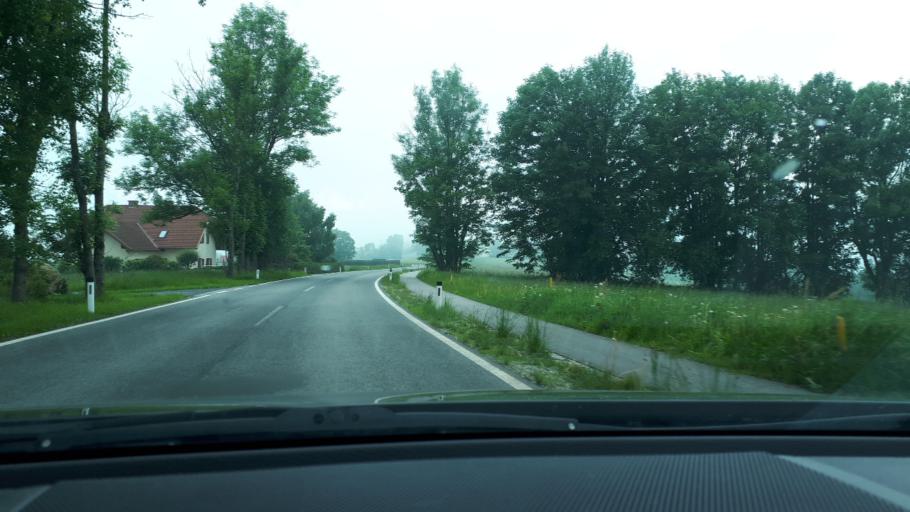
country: AT
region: Carinthia
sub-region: Politischer Bezirk Wolfsberg
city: Preitenegg
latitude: 46.9344
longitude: 14.9411
